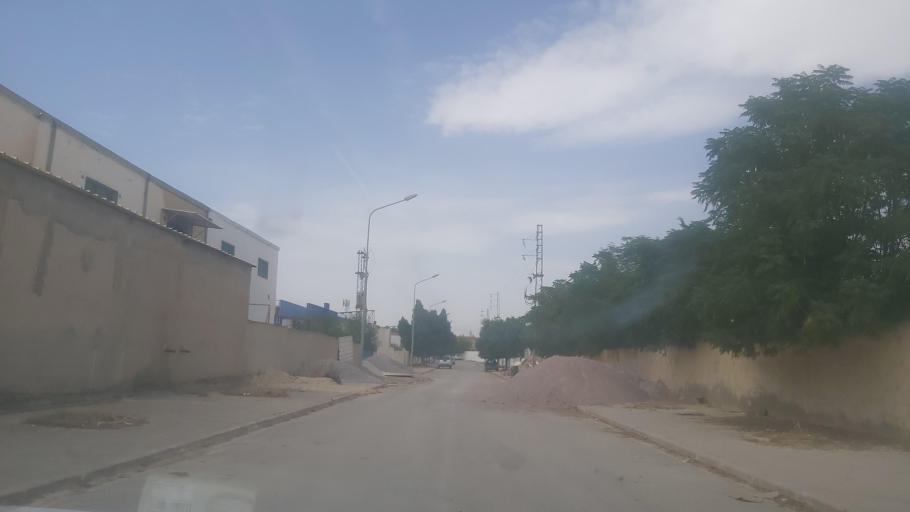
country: TN
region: Silyanah
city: Bu `Aradah
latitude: 36.3533
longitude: 9.6348
